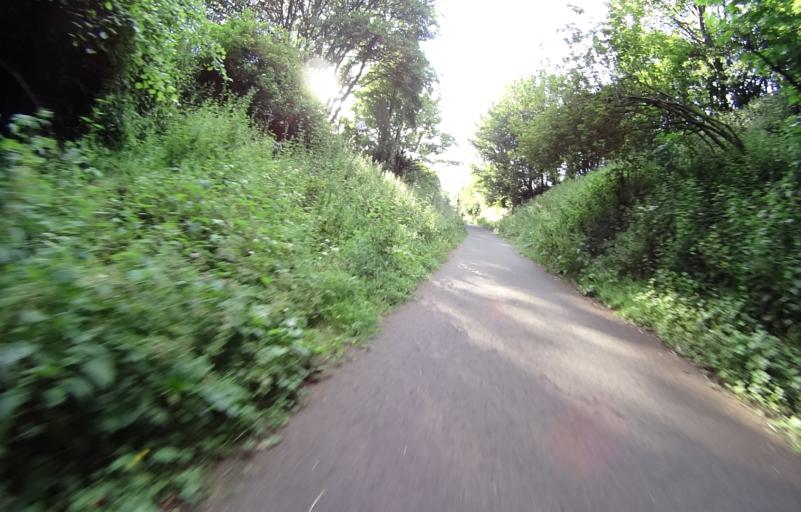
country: GB
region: Scotland
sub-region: Edinburgh
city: Edinburgh
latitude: 55.9520
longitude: -3.2375
